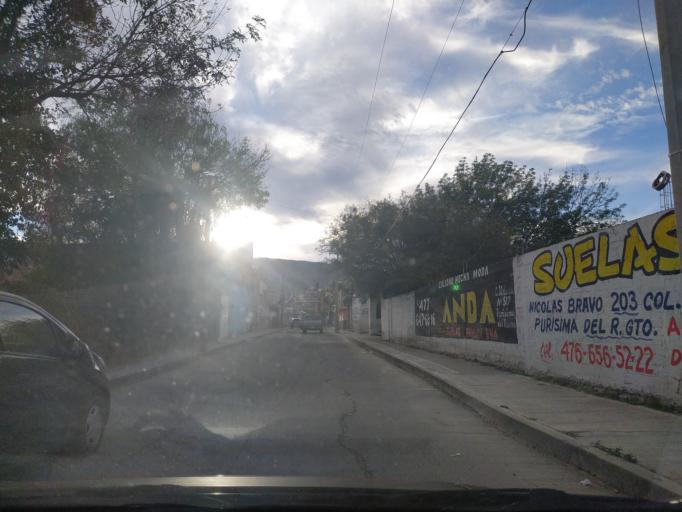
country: LA
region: Oudomxai
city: Muang La
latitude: 21.0333
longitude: 101.8850
